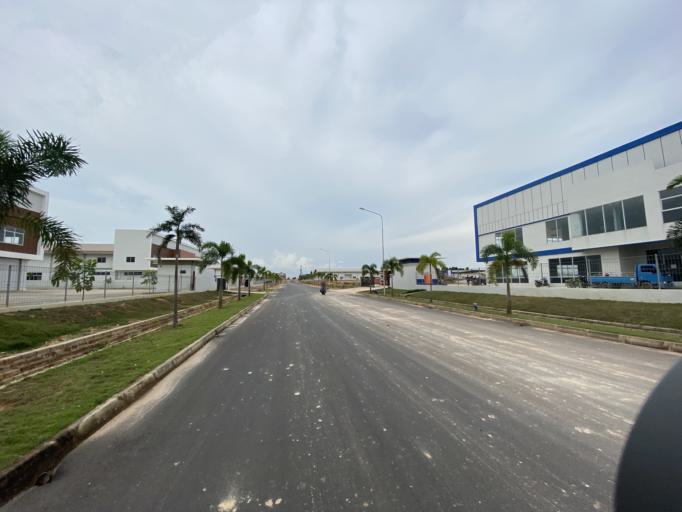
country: SG
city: Singapore
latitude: 1.0214
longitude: 103.9490
